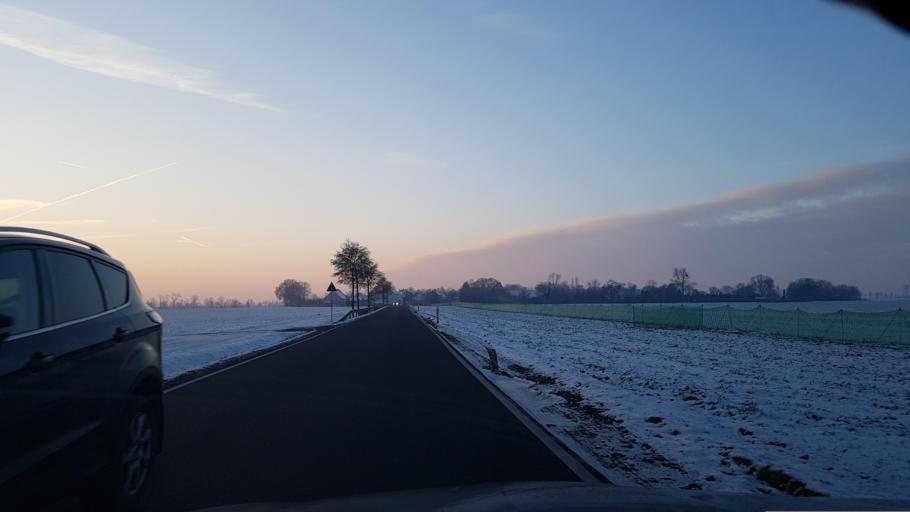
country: DE
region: Saxony
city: Krostitz
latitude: 51.4204
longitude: 12.4602
